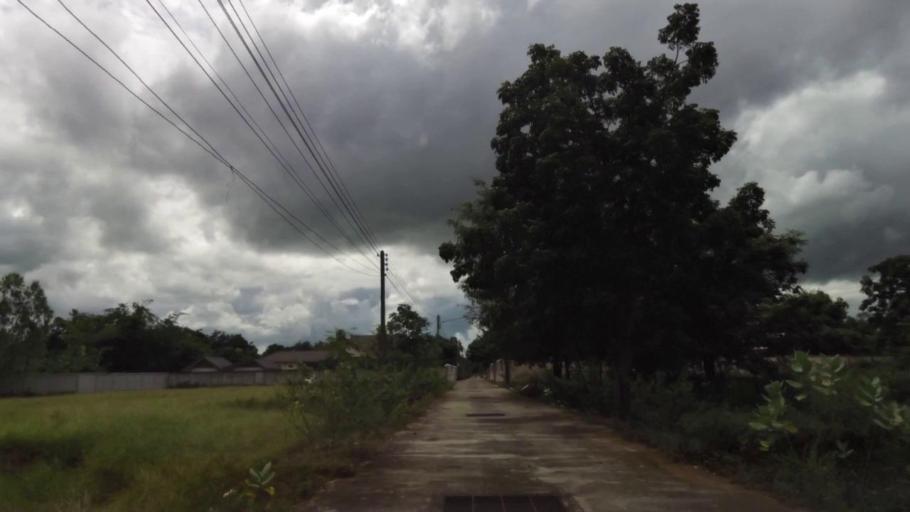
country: TH
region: Nakhon Sawan
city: Phai Sali
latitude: 15.6028
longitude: 100.6592
